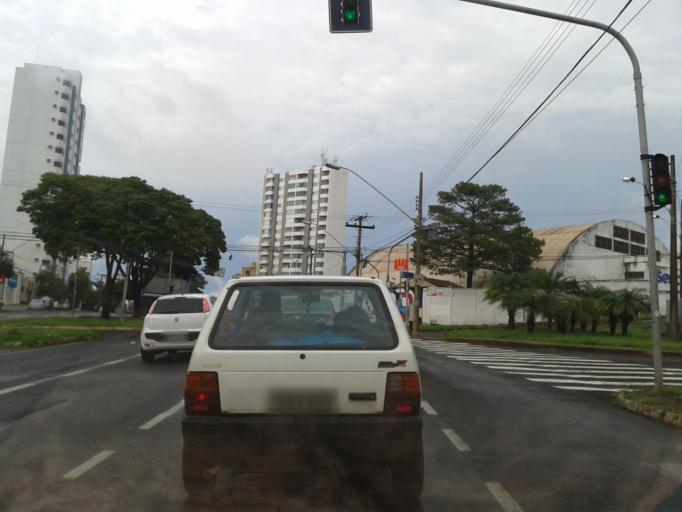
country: BR
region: Minas Gerais
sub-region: Uberlandia
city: Uberlandia
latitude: -18.9114
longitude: -48.2647
